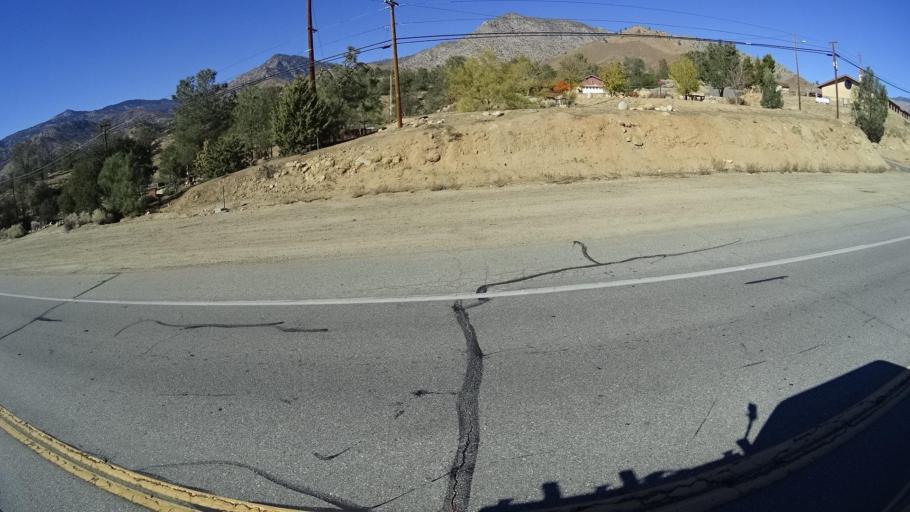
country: US
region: California
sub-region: Kern County
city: Wofford Heights
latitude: 35.7093
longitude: -118.4441
